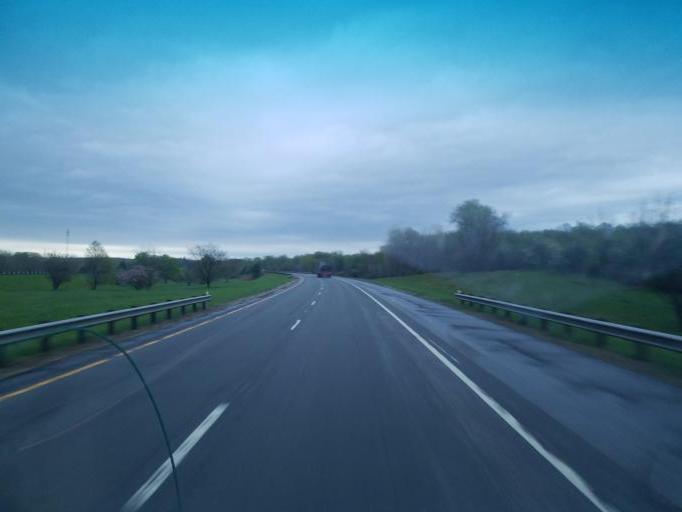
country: US
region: Ohio
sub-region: Medina County
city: Medina
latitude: 41.1623
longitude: -81.7724
